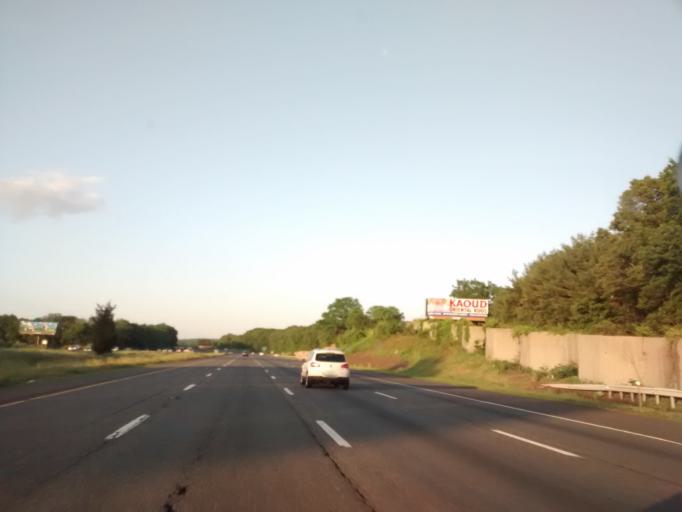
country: US
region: Connecticut
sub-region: Tolland County
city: Rockville
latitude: 41.8283
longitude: -72.4786
